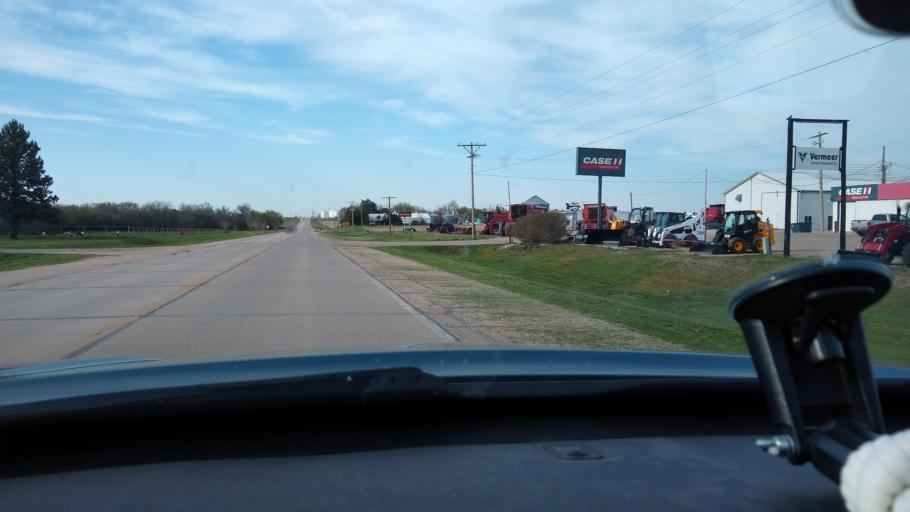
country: US
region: Nebraska
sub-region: Fillmore County
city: Geneva
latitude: 40.5399
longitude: -97.5958
